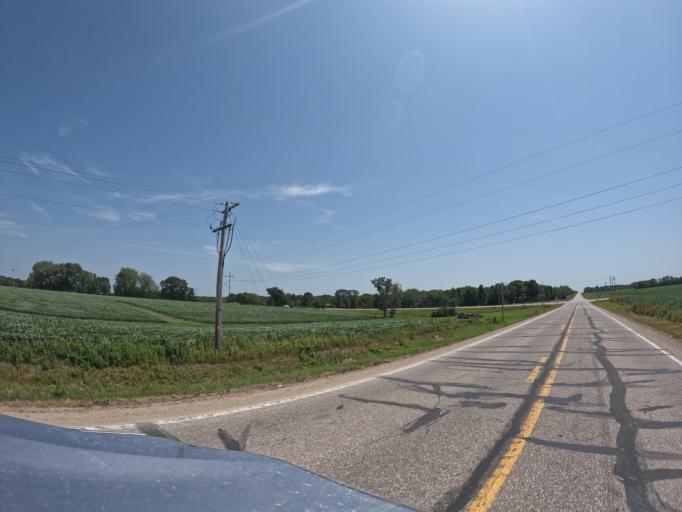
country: US
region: Iowa
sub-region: Henry County
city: Mount Pleasant
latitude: 40.9686
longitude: -91.6124
